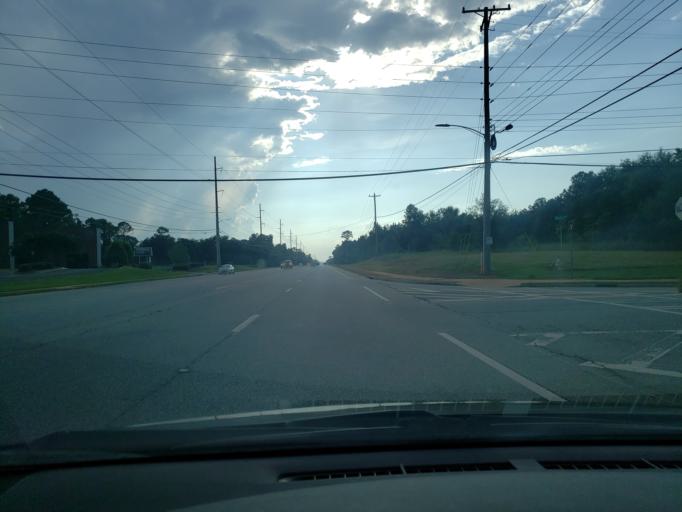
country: US
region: Georgia
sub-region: Dougherty County
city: Albany
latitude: 31.5857
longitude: -84.2375
